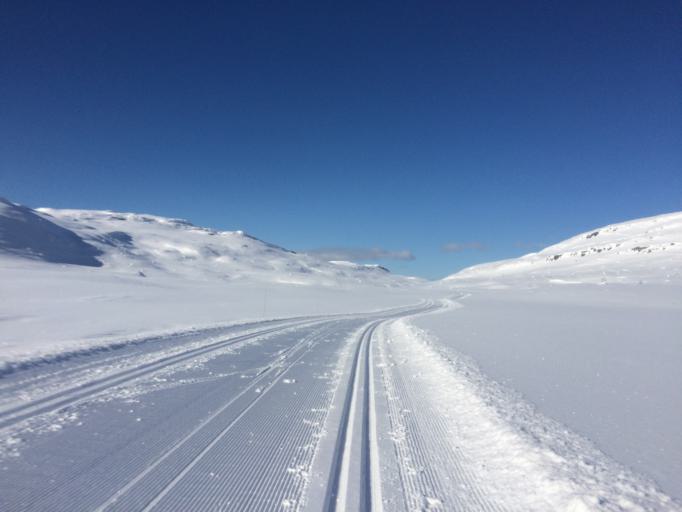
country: NO
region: Oppland
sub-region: Ringebu
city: Ringebu
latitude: 61.3806
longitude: 10.0603
